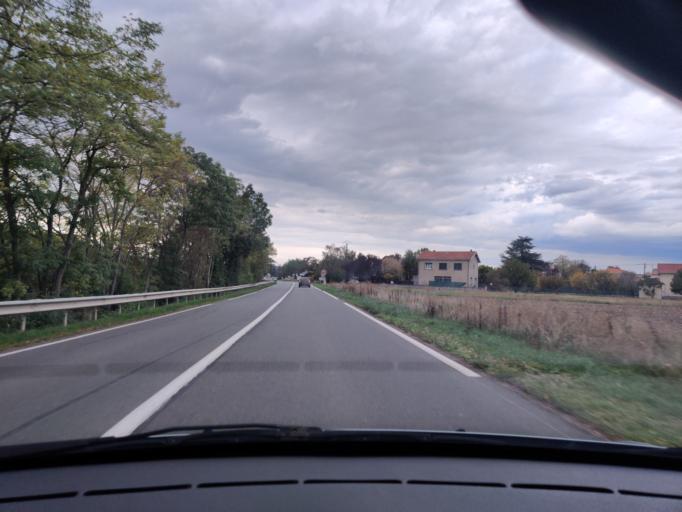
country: FR
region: Auvergne
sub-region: Departement du Puy-de-Dome
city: Saint-Bonnet-pres-Riom
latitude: 45.9234
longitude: 3.1201
